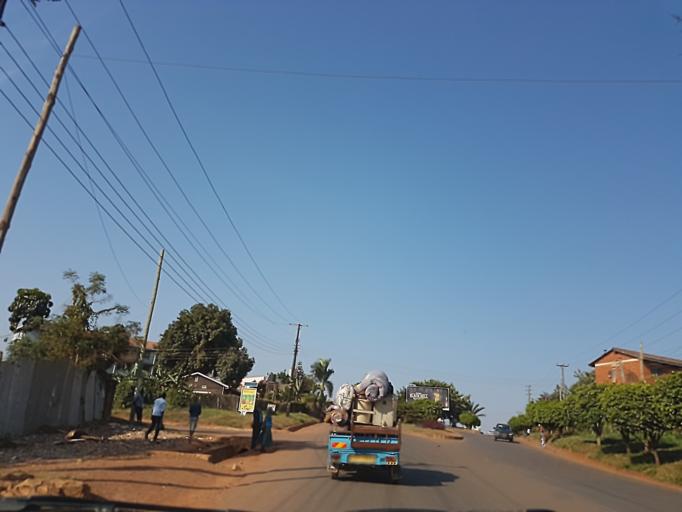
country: UG
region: Central Region
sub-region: Wakiso District
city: Kireka
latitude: 0.3449
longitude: 32.6169
